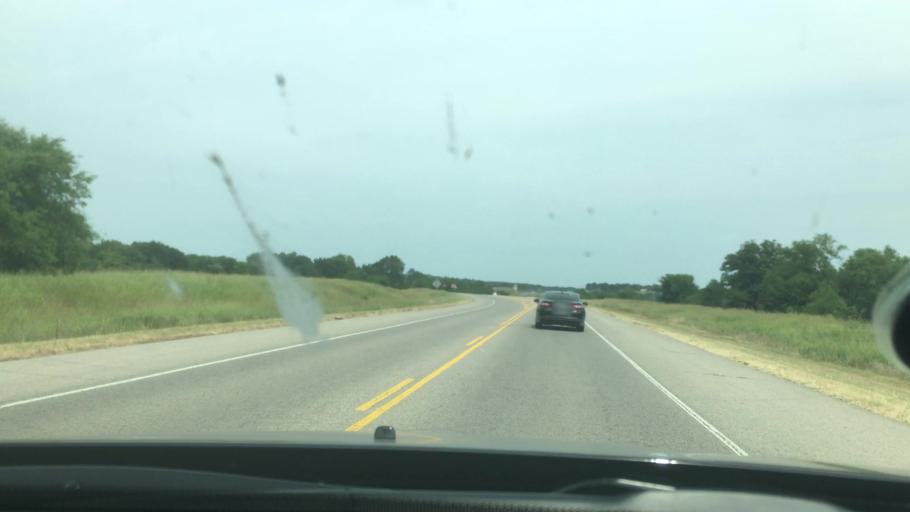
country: US
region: Oklahoma
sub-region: Pontotoc County
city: Ada
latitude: 34.7176
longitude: -96.6249
